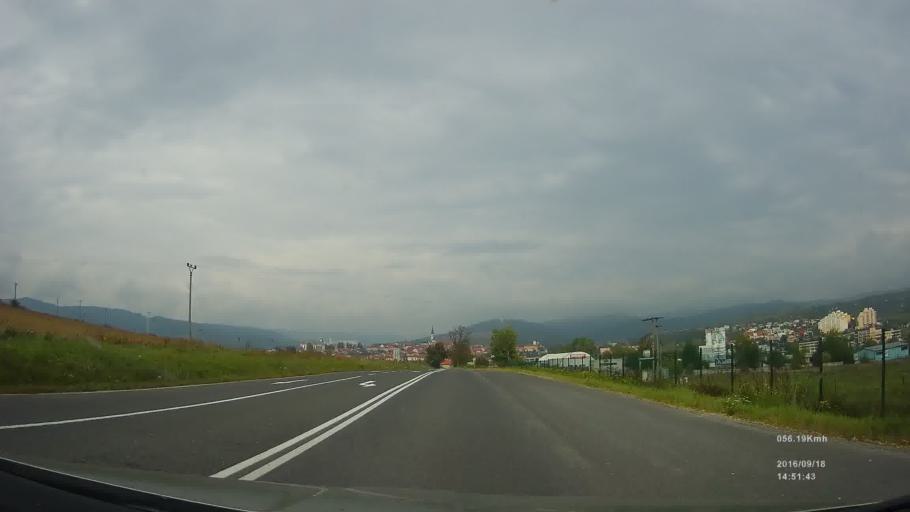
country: SK
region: Presovsky
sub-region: Okres Presov
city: Levoca
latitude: 49.0116
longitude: 20.5861
